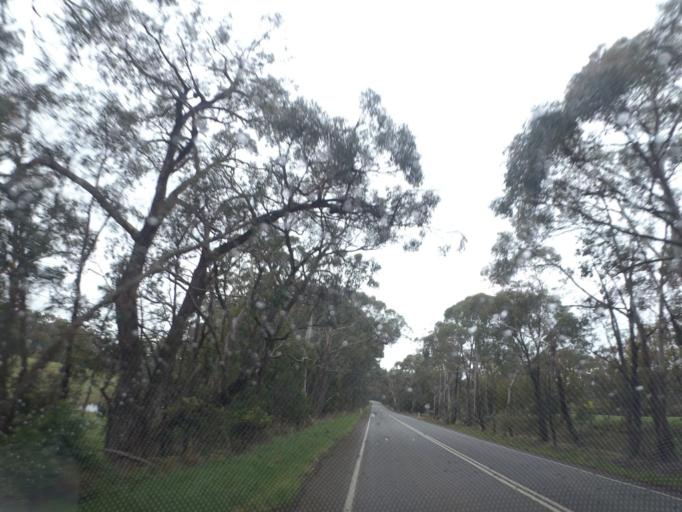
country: AU
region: Victoria
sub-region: Hume
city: Sunbury
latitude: -37.3449
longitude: 144.6814
